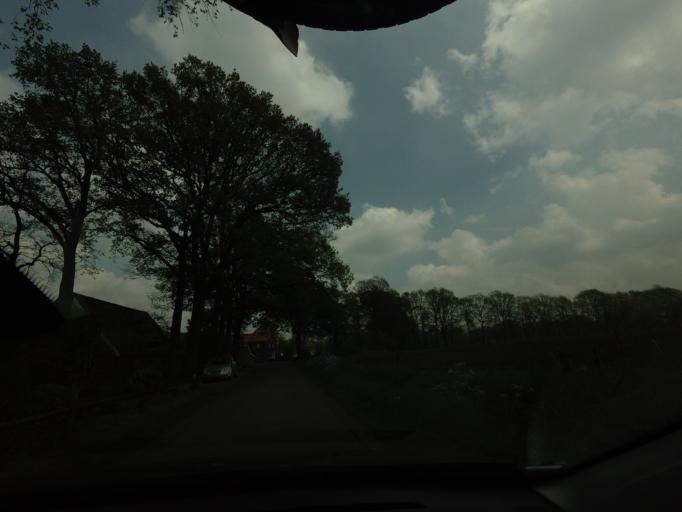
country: NL
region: Gelderland
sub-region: Oost Gelre
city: Lichtenvoorde
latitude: 52.0113
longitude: 6.6012
